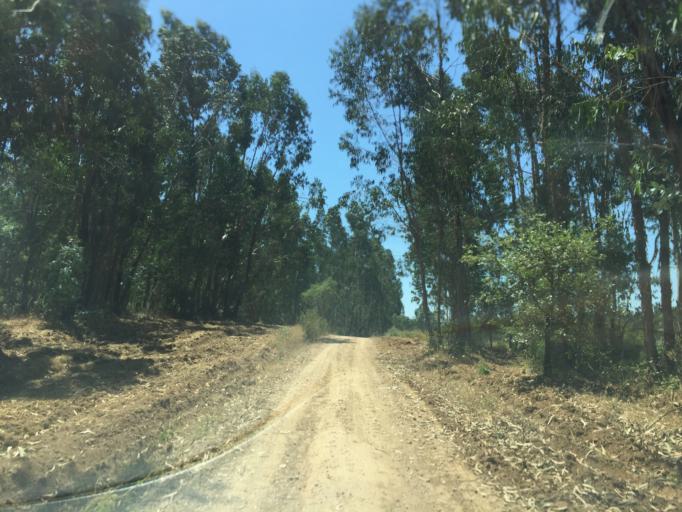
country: PT
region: Santarem
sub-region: Tomar
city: Tomar
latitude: 39.6032
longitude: -8.3582
